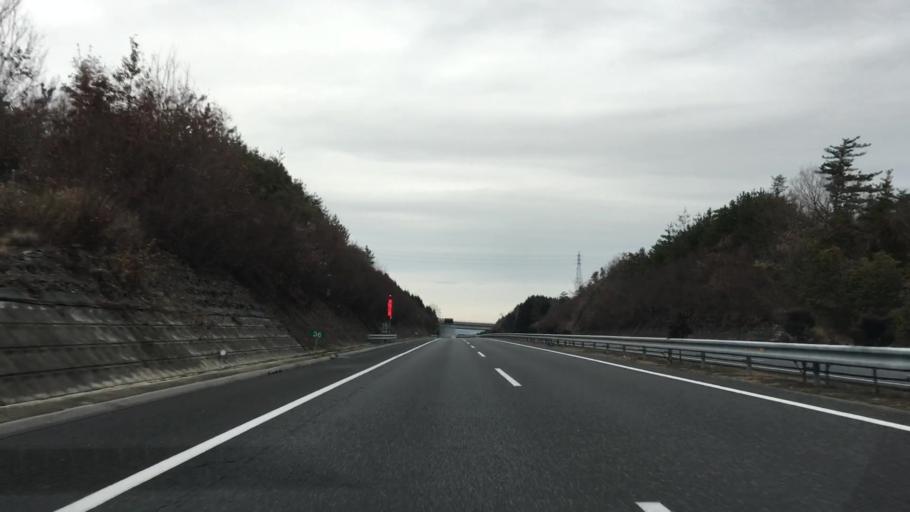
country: JP
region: Gifu
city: Toki
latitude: 35.3249
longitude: 137.1759
